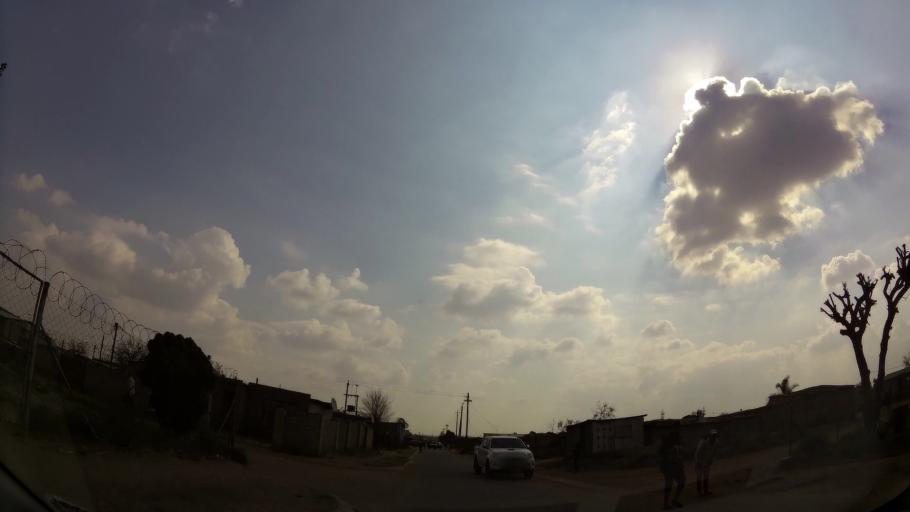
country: ZA
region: Gauteng
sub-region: Ekurhuleni Metropolitan Municipality
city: Springs
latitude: -26.1301
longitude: 28.4803
